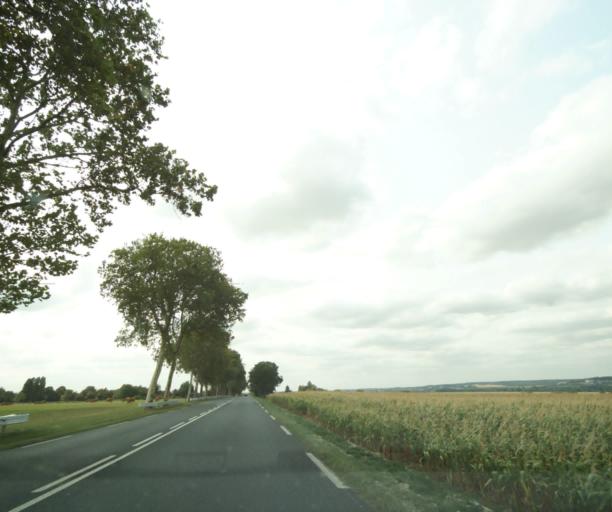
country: FR
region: Centre
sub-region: Departement de l'Indre
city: Buzancais
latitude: 46.9125
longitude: 1.3298
